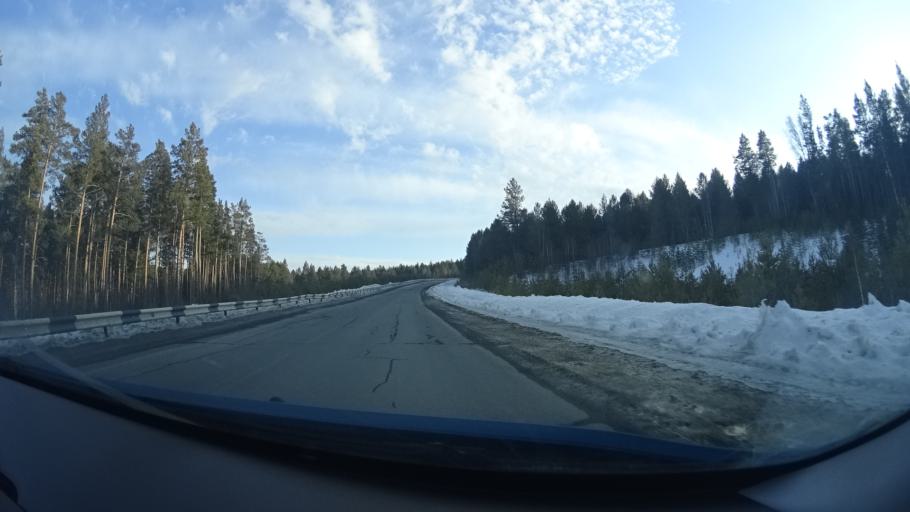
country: RU
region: Bashkortostan
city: Lomovka
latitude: 53.6000
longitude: 58.2014
